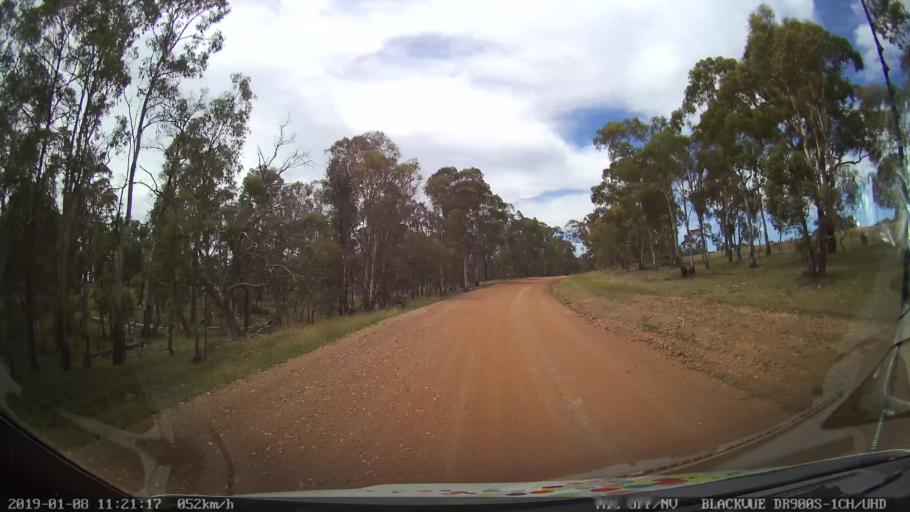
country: AU
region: New South Wales
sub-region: Guyra
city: Guyra
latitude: -30.2362
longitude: 151.5660
